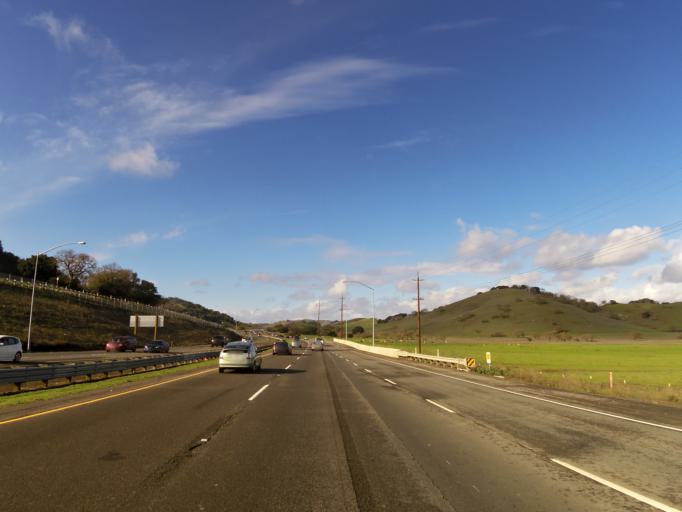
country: US
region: California
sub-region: Marin County
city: Novato
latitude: 38.1649
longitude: -122.5773
